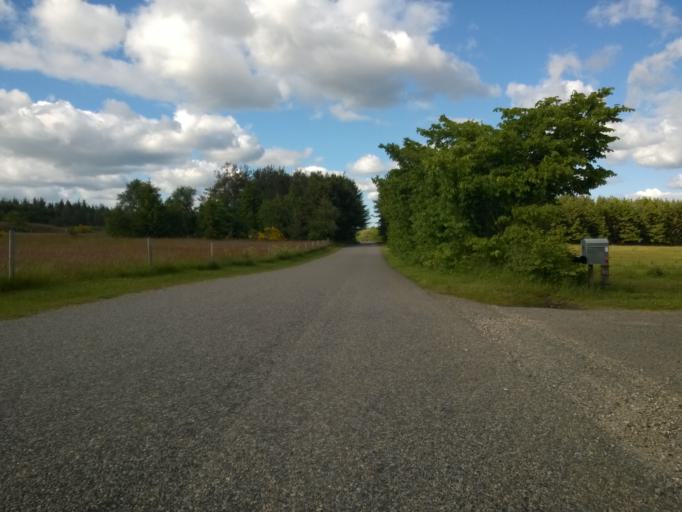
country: DK
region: Central Jutland
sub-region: Holstebro Kommune
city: Vinderup
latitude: 56.5000
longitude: 8.8390
